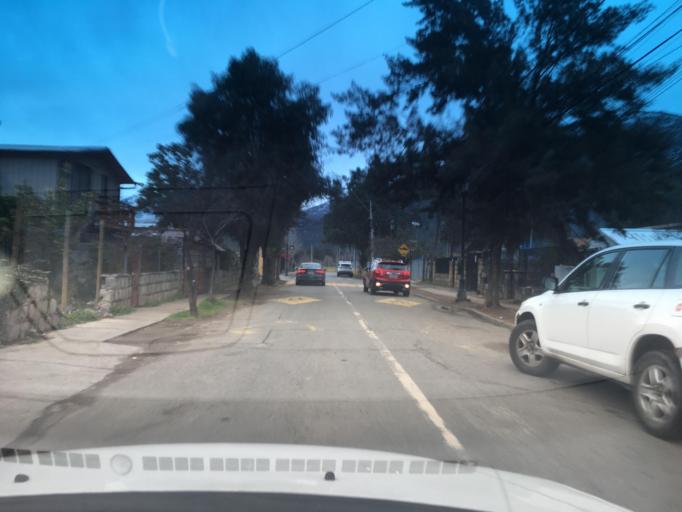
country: CL
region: Santiago Metropolitan
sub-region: Provincia de Cordillera
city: Puente Alto
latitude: -33.6428
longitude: -70.3547
